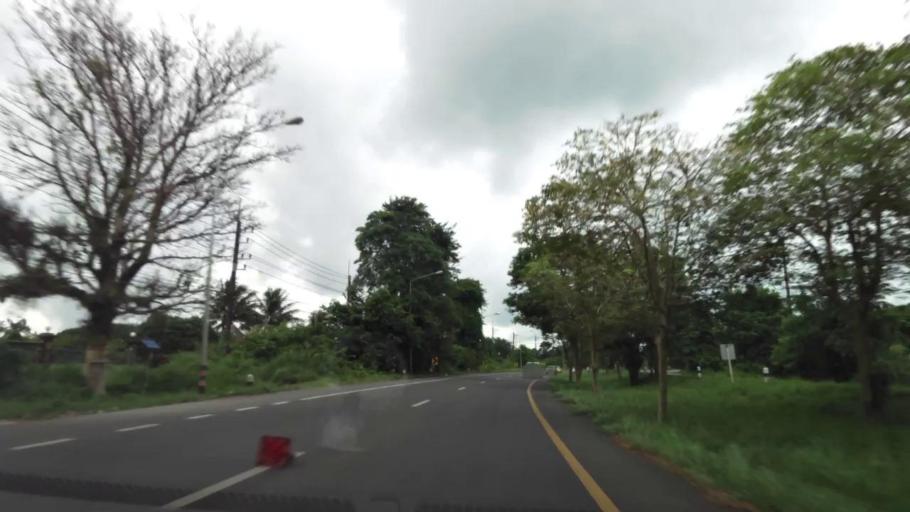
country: TH
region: Chanthaburi
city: Tha Mai
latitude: 12.6756
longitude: 102.0050
